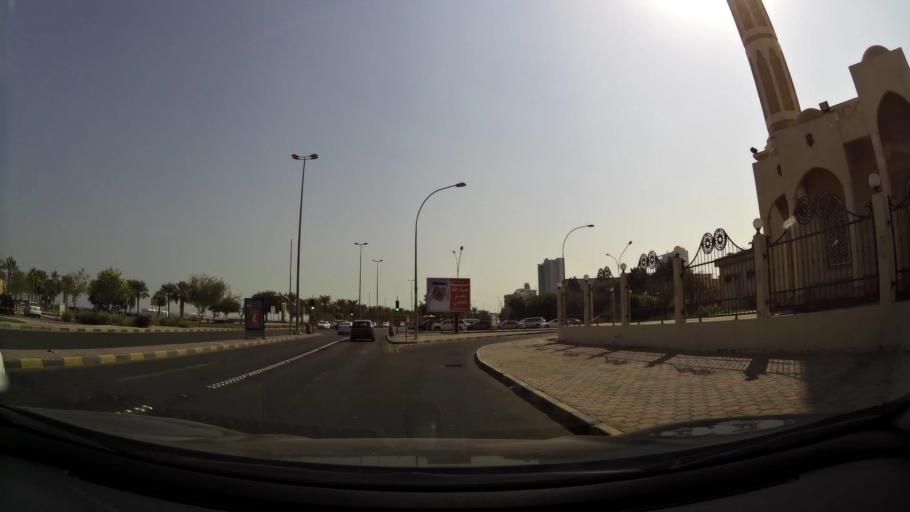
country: KW
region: Al Ahmadi
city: Al Fahahil
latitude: 29.0859
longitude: 48.1389
